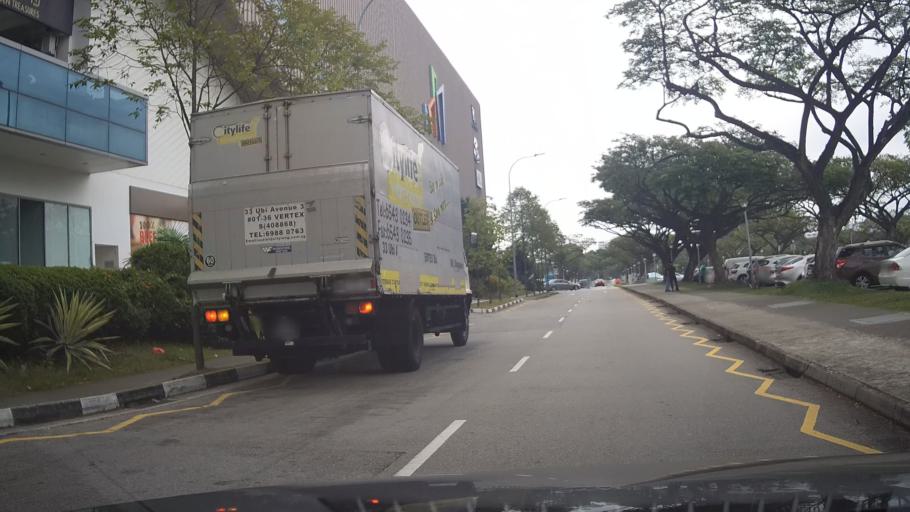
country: SG
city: Singapore
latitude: 1.3013
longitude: 103.8765
